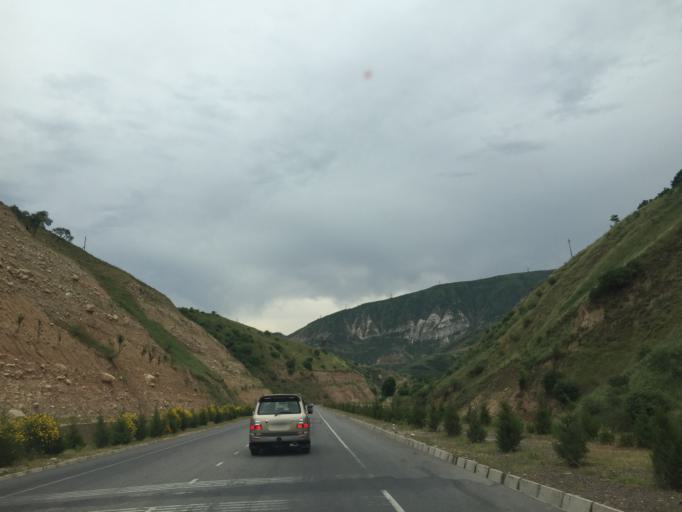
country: TJ
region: Khatlon
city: Norak
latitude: 38.4503
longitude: 69.2016
